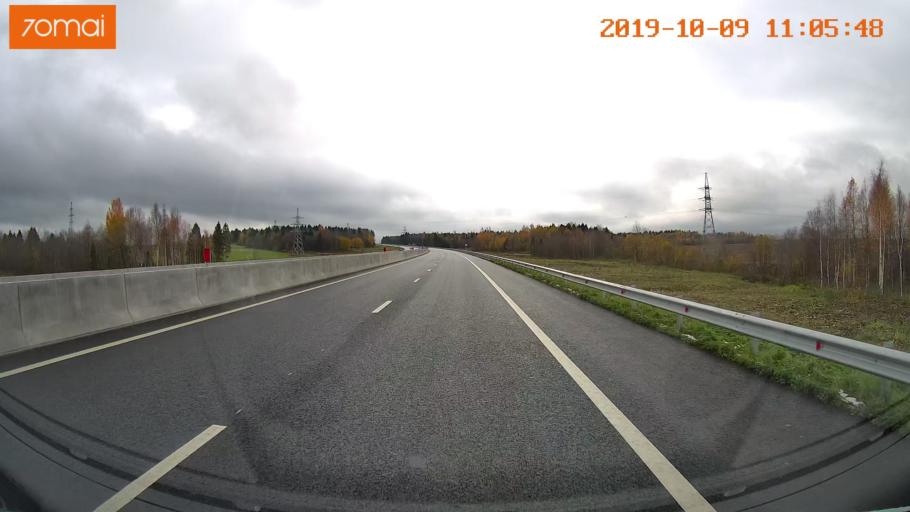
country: RU
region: Vologda
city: Molochnoye
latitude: 59.1948
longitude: 39.7580
